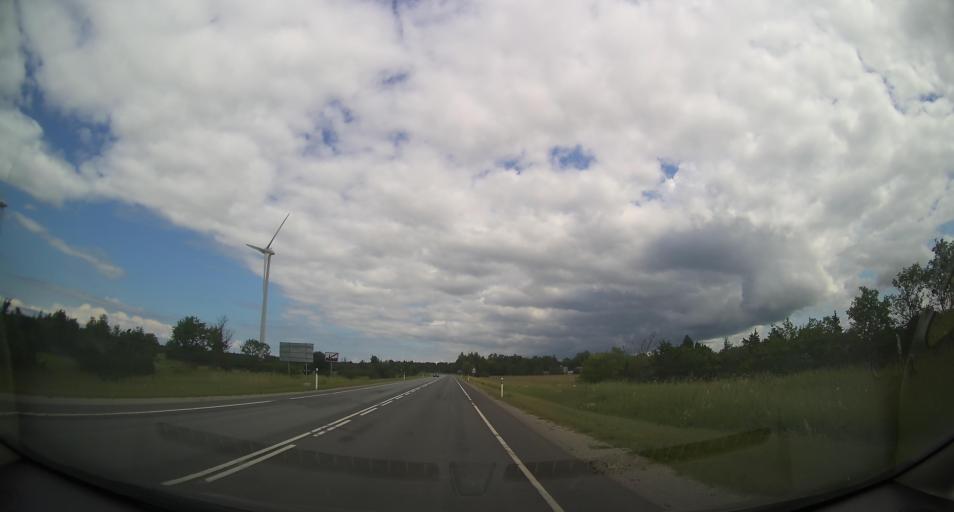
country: EE
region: Laeaene
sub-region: Lihula vald
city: Lihula
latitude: 58.5873
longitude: 23.5299
